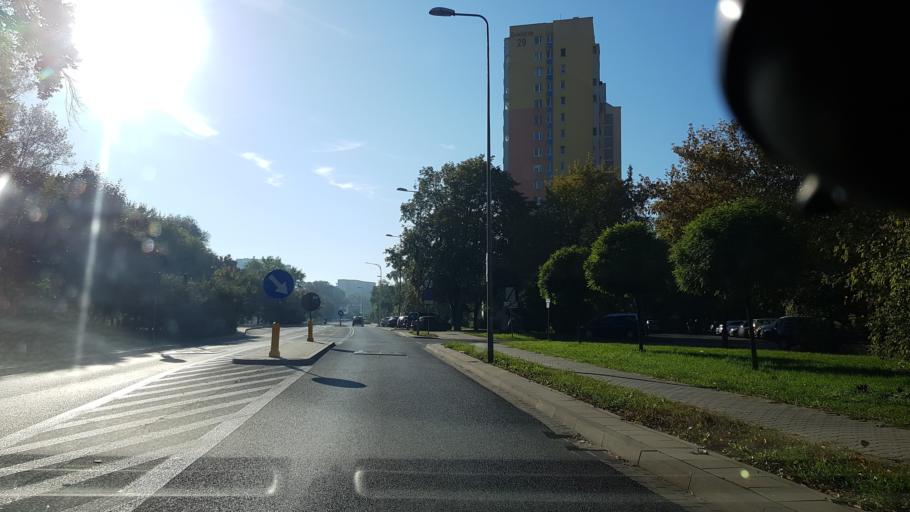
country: PL
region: Masovian Voivodeship
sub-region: Warszawa
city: Zoliborz
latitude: 52.2863
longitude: 20.9777
